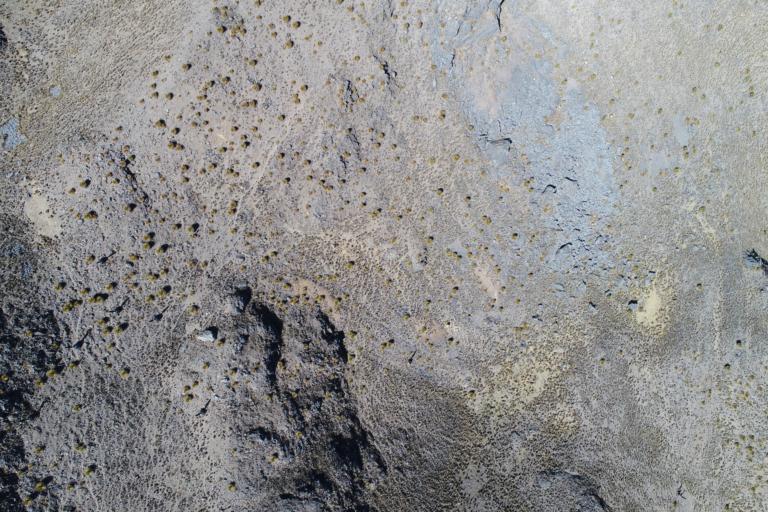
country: BO
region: La Paz
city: Viloco
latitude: -16.8097
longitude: -67.5446
